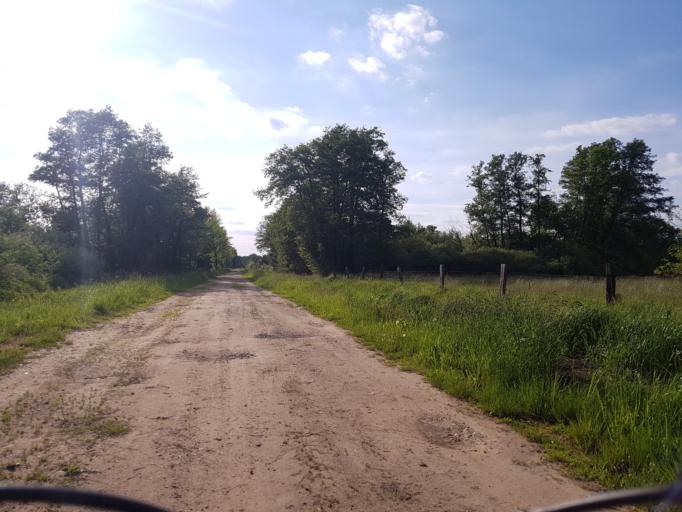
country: DE
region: Brandenburg
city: Groden
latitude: 51.4169
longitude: 13.5581
